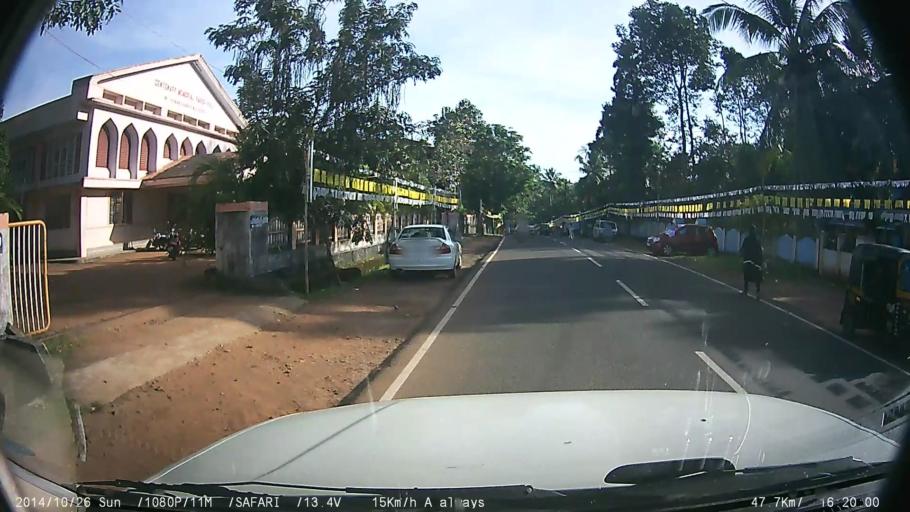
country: IN
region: Kerala
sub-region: Kottayam
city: Changanacheri
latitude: 9.4230
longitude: 76.5622
